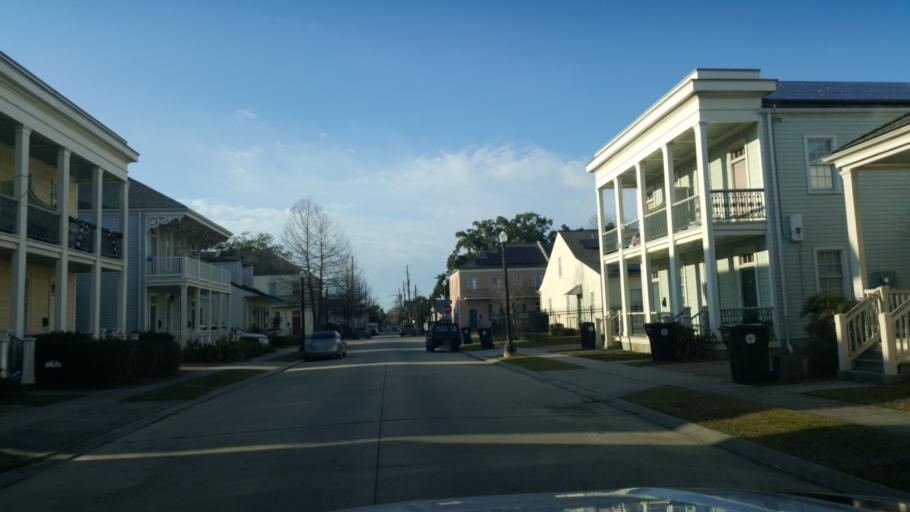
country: US
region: Louisiana
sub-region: Jefferson Parish
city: Gretna
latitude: 29.9296
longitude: -90.0718
